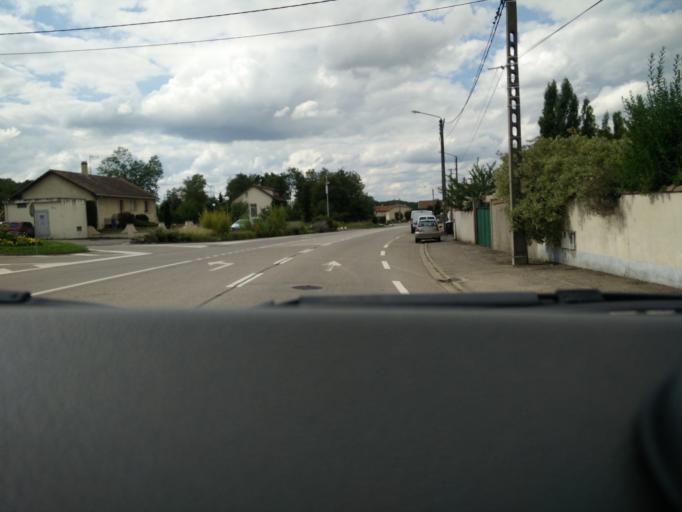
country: FR
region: Lorraine
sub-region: Departement de Meurthe-et-Moselle
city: Saint-Nicolas-de-Port
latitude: 48.6348
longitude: 6.2896
